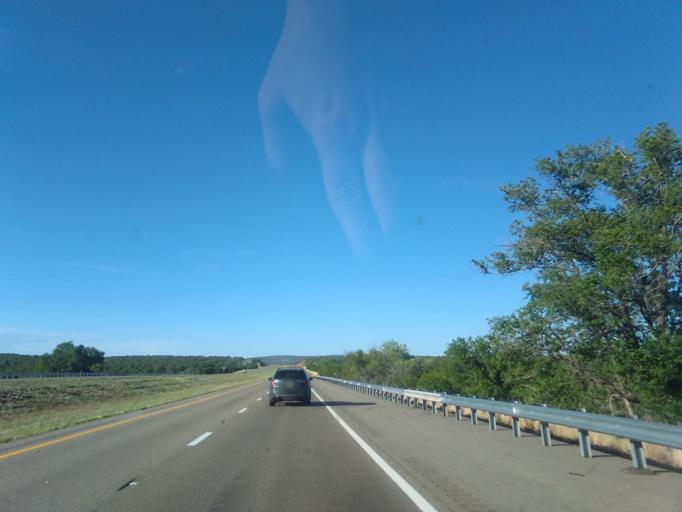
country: US
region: New Mexico
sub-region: San Miguel County
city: Las Vegas
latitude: 35.4379
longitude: -105.2883
